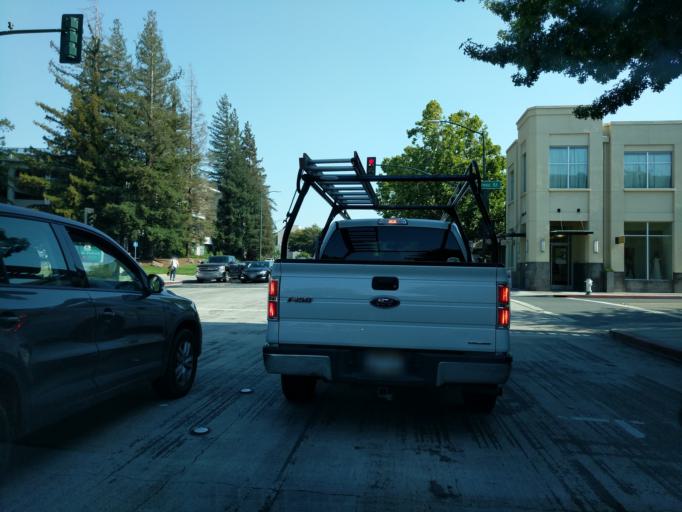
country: US
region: California
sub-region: Contra Costa County
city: Walnut Creek
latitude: 37.8996
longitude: -122.0599
